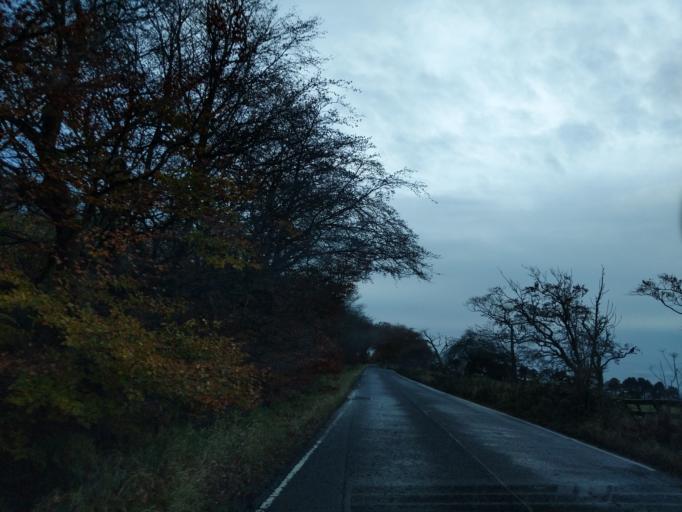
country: GB
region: Scotland
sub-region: West Lothian
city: Linlithgow
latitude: 55.9394
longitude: -3.6216
